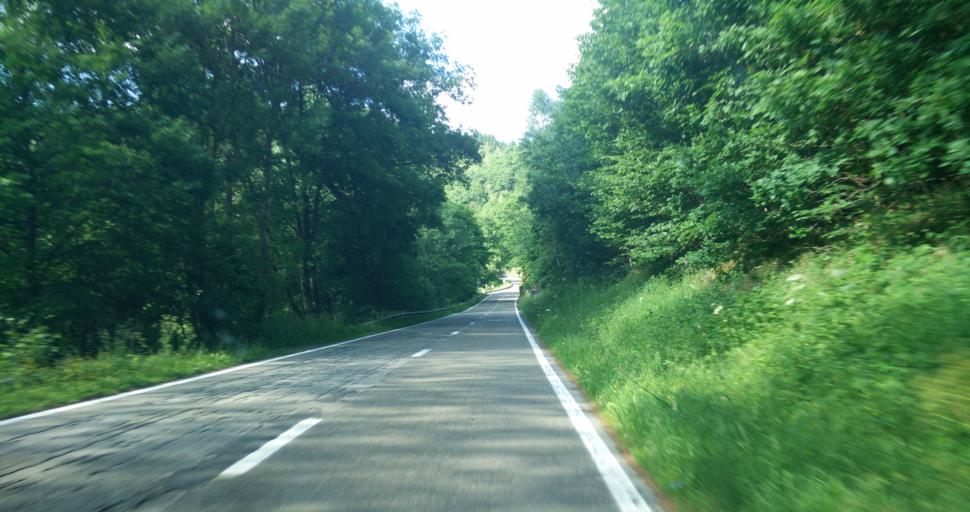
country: BE
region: Wallonia
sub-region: Province du Luxembourg
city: Houffalize
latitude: 50.1351
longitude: 5.7221
